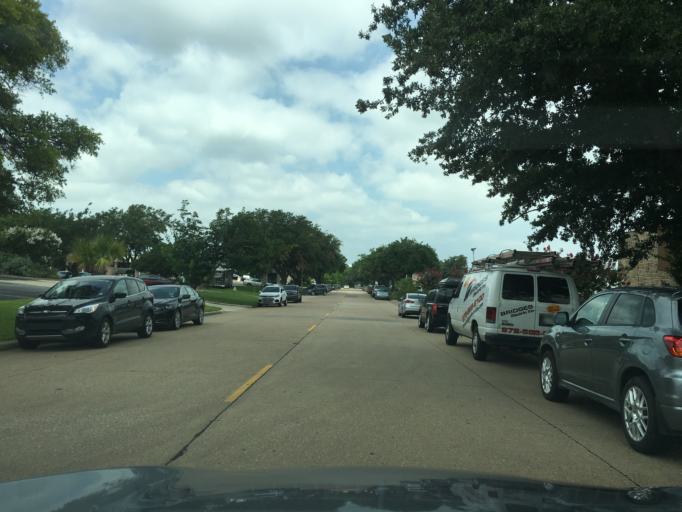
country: US
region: Texas
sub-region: Dallas County
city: Addison
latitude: 32.9371
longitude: -96.8332
